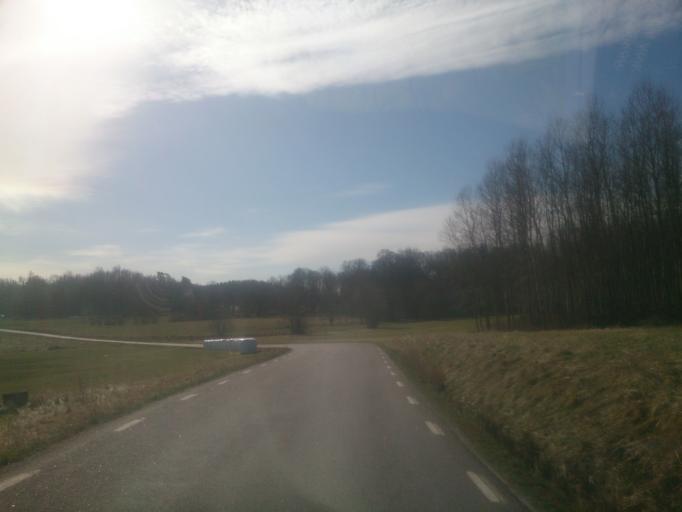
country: SE
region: OEstergoetland
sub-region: Linkopings Kommun
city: Sturefors
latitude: 58.2955
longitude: 15.8503
